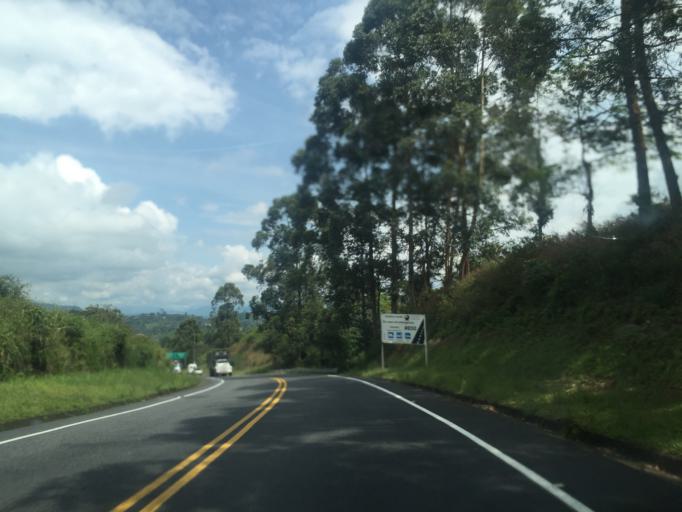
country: CO
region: Caldas
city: Chinchina
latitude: 4.9389
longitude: -75.6208
